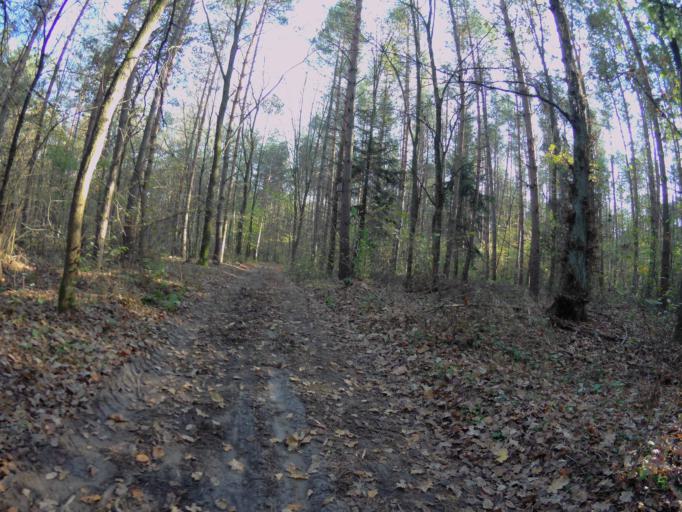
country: PL
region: Subcarpathian Voivodeship
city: Nowa Sarzyna
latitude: 50.3098
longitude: 22.3494
